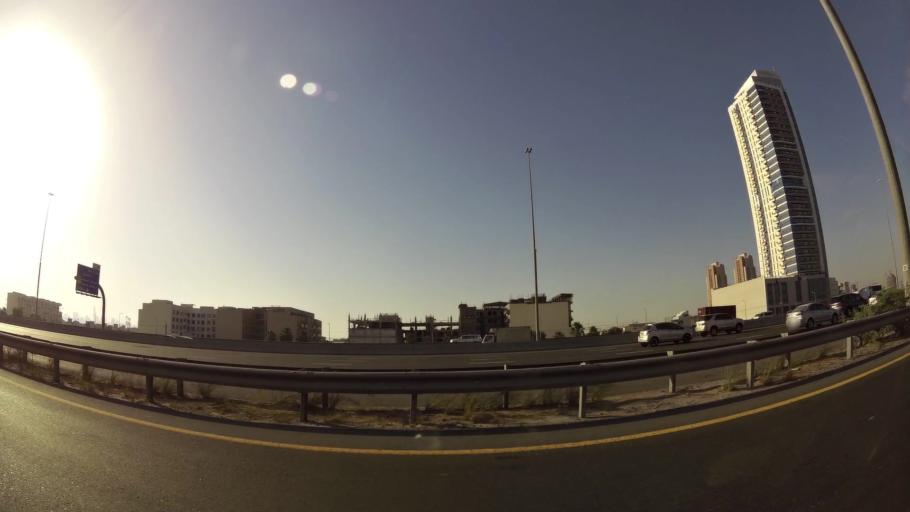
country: AE
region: Dubai
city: Dubai
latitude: 25.0415
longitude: 55.1927
